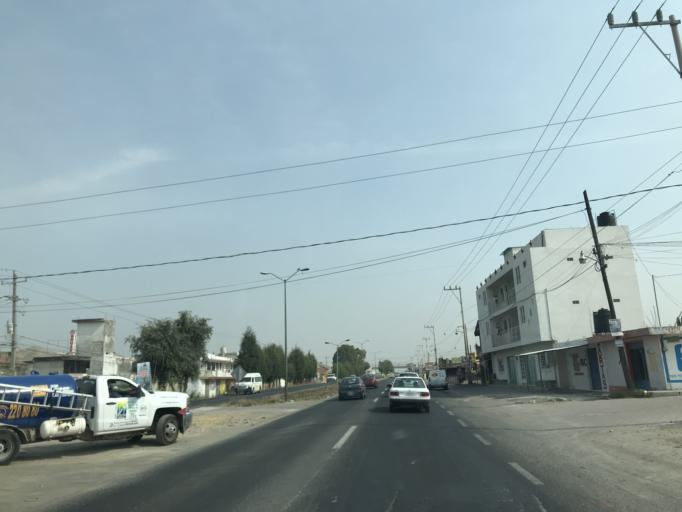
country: MX
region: Tlaxcala
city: Tenancingo
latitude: 19.1445
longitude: -98.1918
